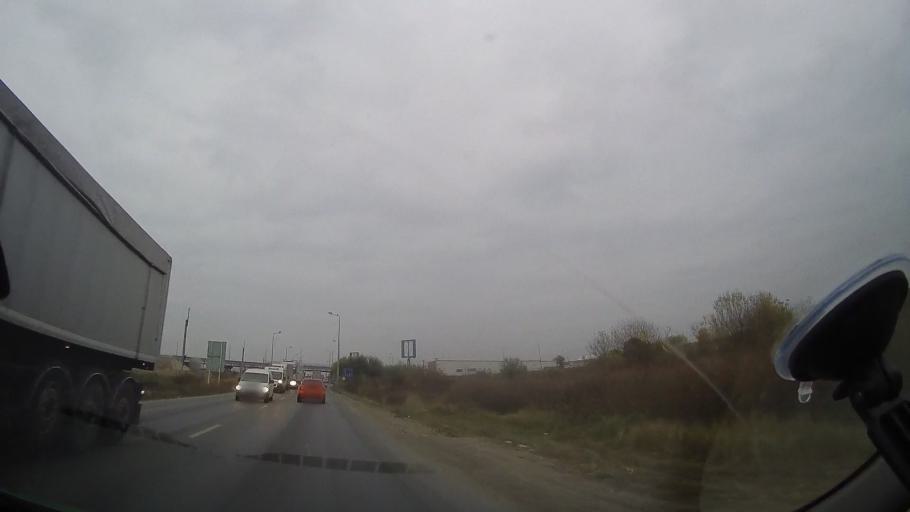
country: RO
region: Ilfov
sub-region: Comuna Glina
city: Catelu
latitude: 44.4042
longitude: 26.2321
